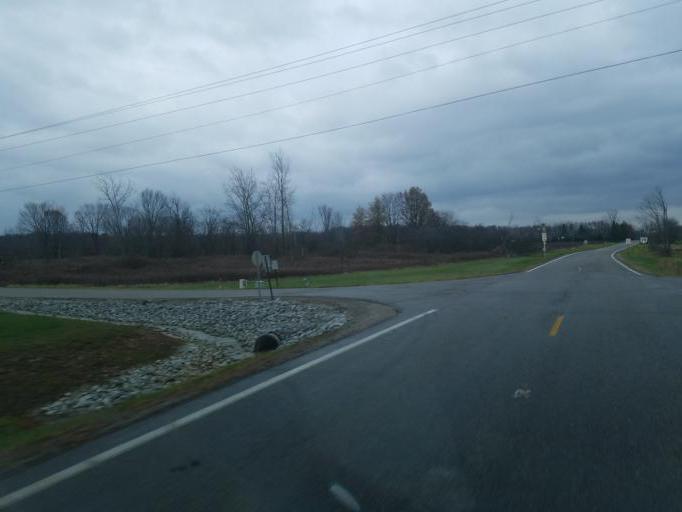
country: US
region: Ohio
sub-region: Crawford County
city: Galion
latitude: 40.6395
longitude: -82.7658
